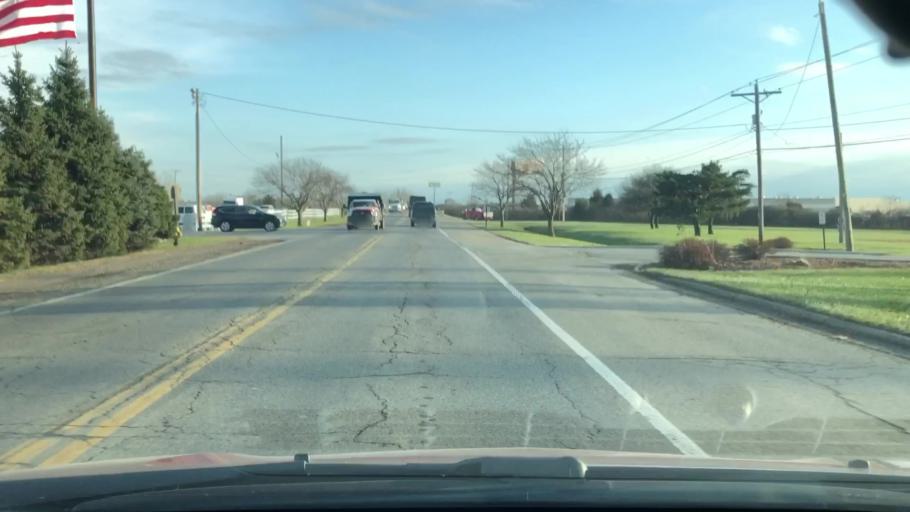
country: US
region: Ohio
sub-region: Franklin County
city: Obetz
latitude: 39.8734
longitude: -82.9437
